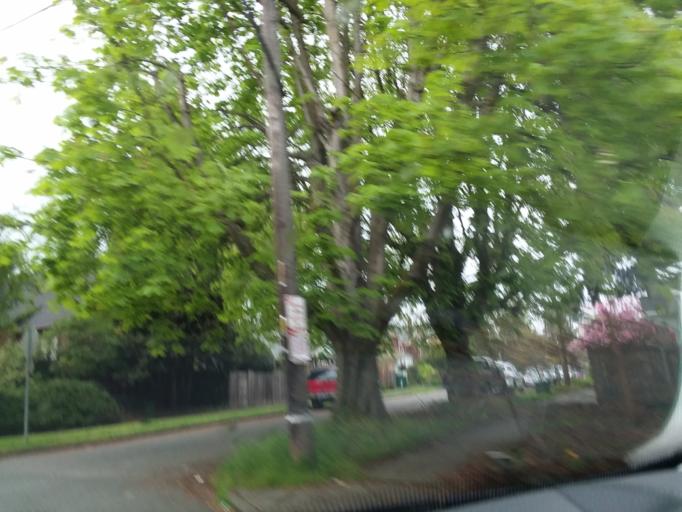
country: US
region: Washington
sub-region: King County
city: Seattle
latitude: 47.6699
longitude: -122.3006
